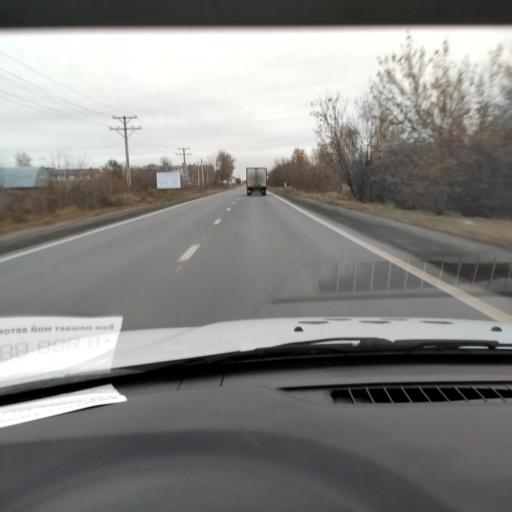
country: RU
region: Samara
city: Tol'yatti
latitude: 53.5553
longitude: 49.3660
